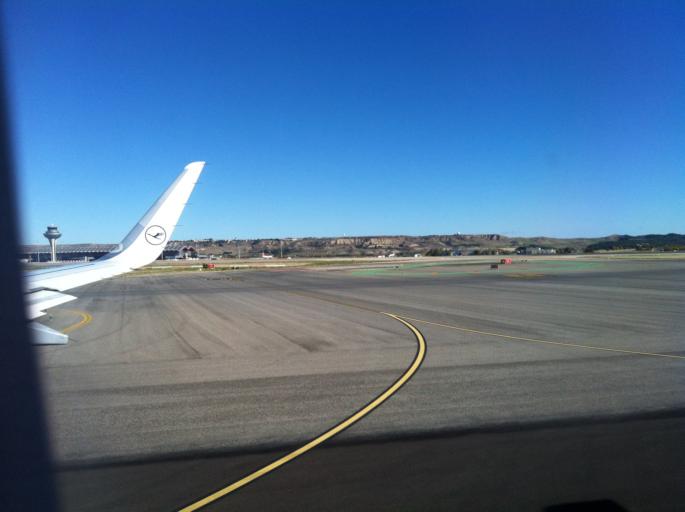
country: ES
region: Madrid
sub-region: Provincia de Madrid
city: Barajas de Madrid
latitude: 40.4843
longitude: -3.5792
